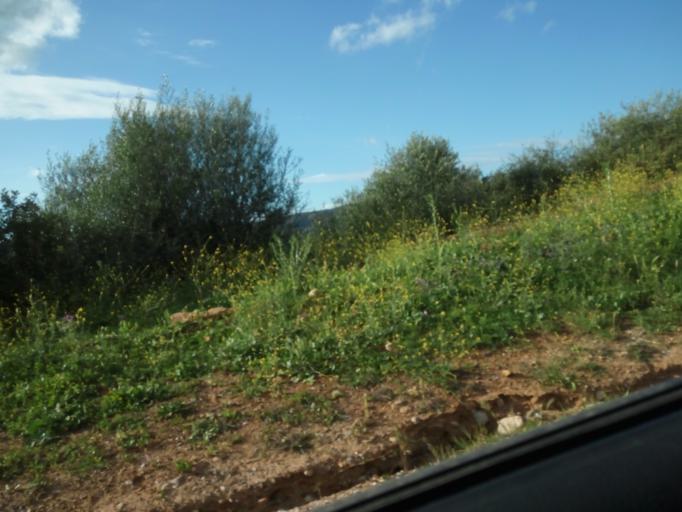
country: DZ
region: Tipaza
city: El Affroun
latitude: 36.3735
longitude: 2.5078
